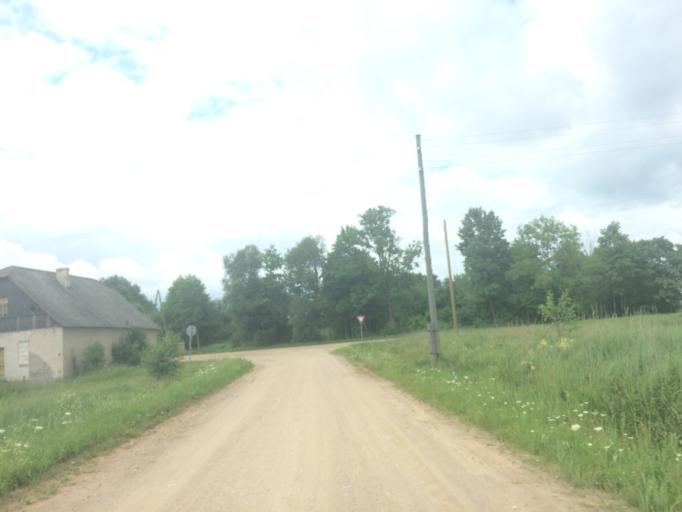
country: LV
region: Rezekne
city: Rezekne
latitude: 56.6626
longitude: 27.2697
